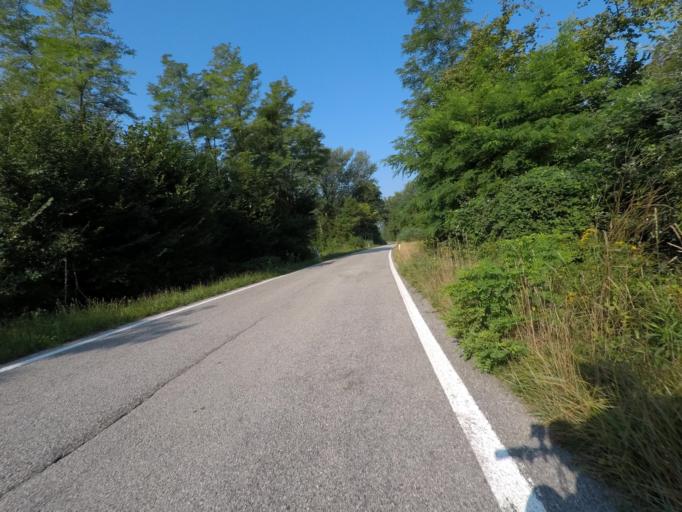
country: IT
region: Friuli Venezia Giulia
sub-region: Provincia di Udine
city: Forgaria nel Friuli
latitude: 46.2128
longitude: 12.9886
